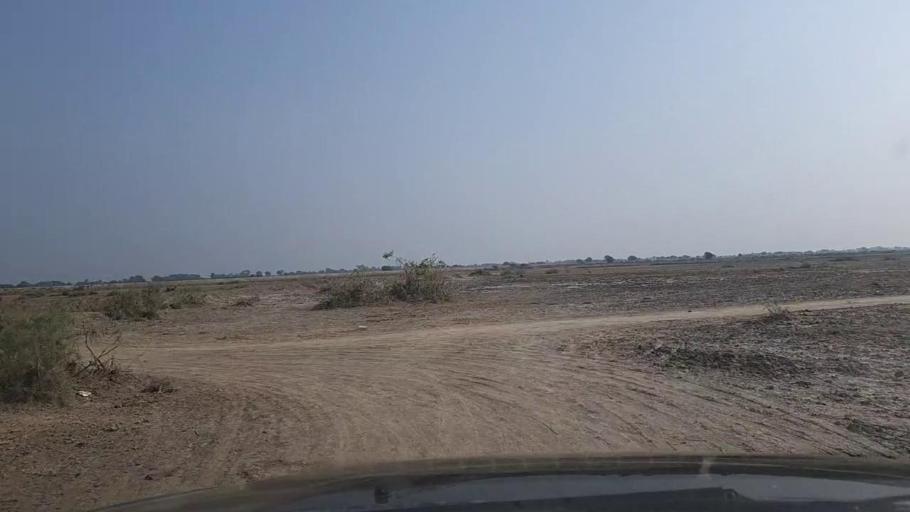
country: PK
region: Sindh
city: Mirpur Batoro
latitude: 24.6762
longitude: 68.2465
